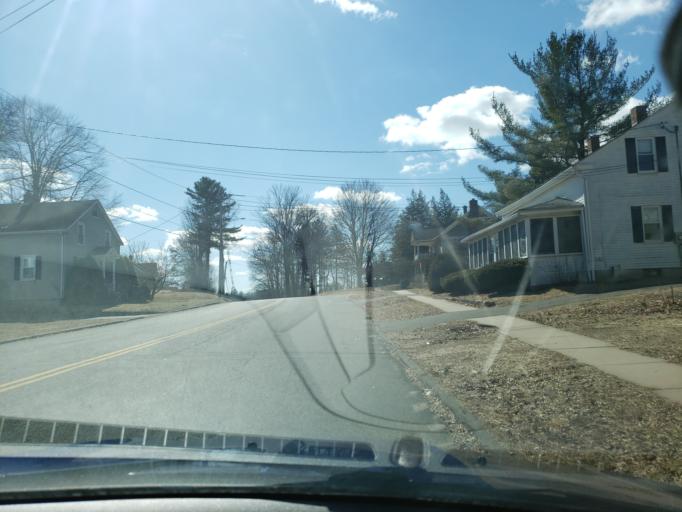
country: US
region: Connecticut
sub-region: Hartford County
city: Hazardville
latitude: 41.9858
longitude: -72.5397
